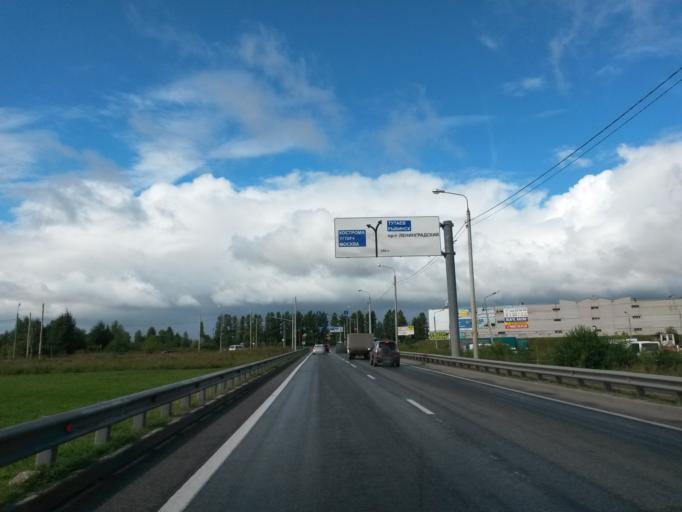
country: RU
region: Jaroslavl
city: Yaroslavl
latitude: 57.6711
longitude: 39.7768
